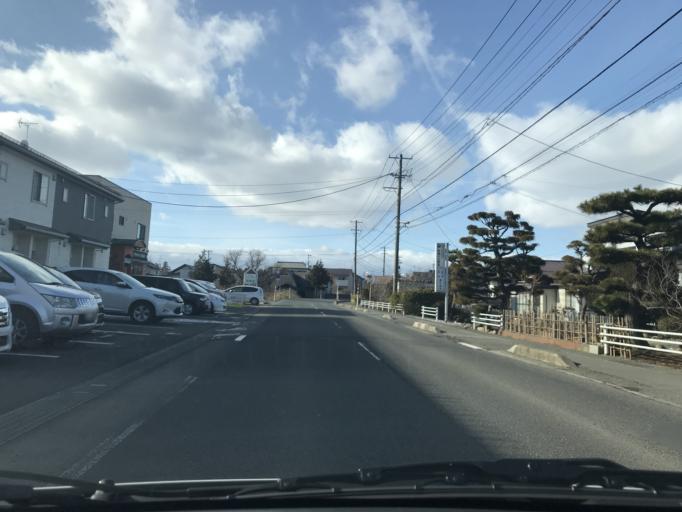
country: JP
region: Iwate
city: Kitakami
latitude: 39.3028
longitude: 141.1016
